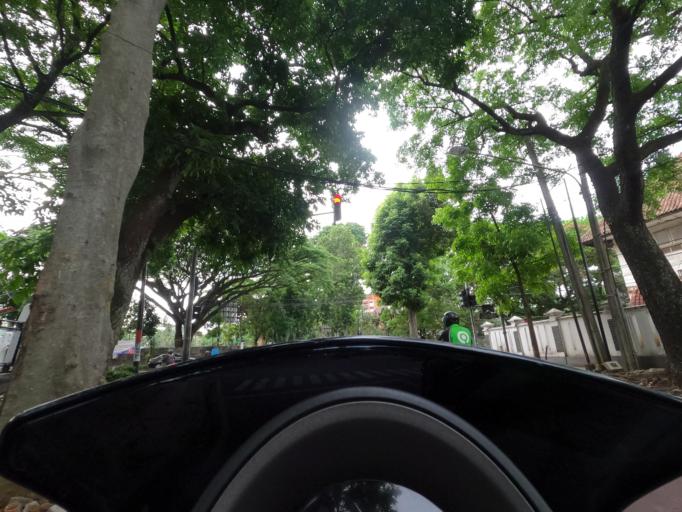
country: ID
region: West Java
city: Bandung
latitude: -6.9095
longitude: 107.6174
